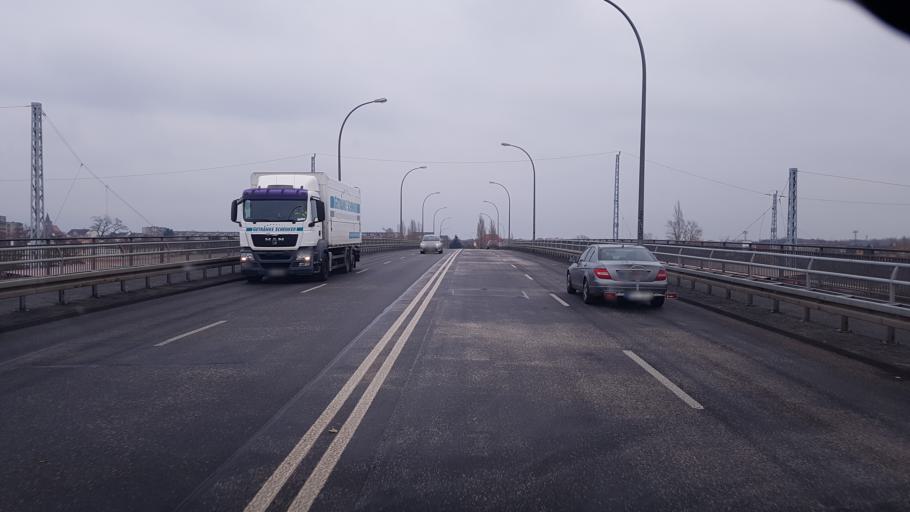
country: DE
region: Brandenburg
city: Eisenhuettenstadt
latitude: 52.1413
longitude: 14.6558
